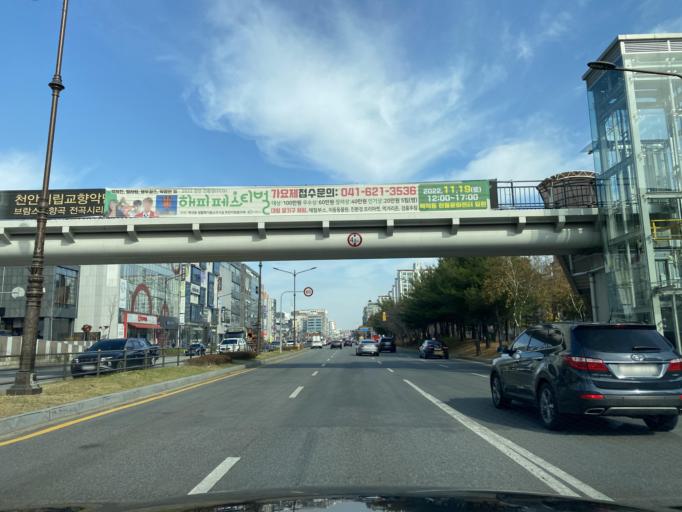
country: KR
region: Chungcheongnam-do
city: Cheonan
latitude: 36.8048
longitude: 127.1064
